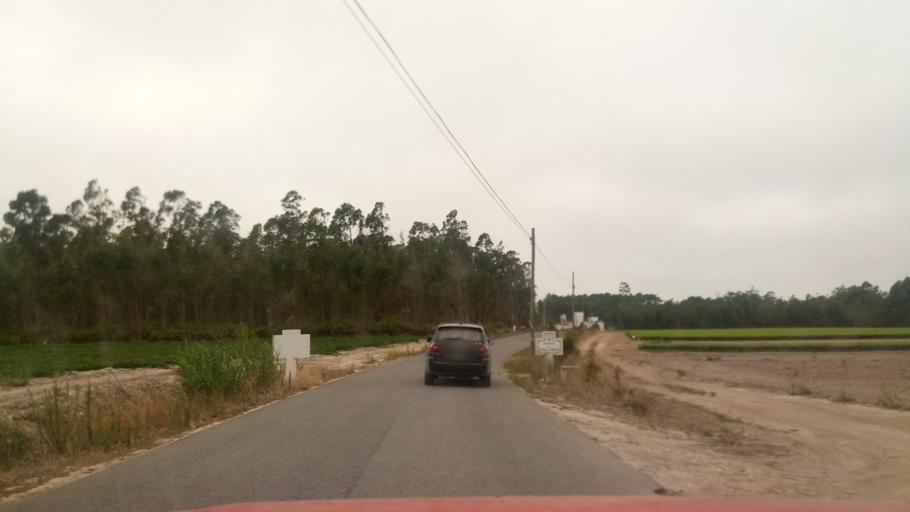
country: PT
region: Leiria
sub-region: Caldas da Rainha
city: Caldas da Rainha
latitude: 39.4422
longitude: -9.1623
